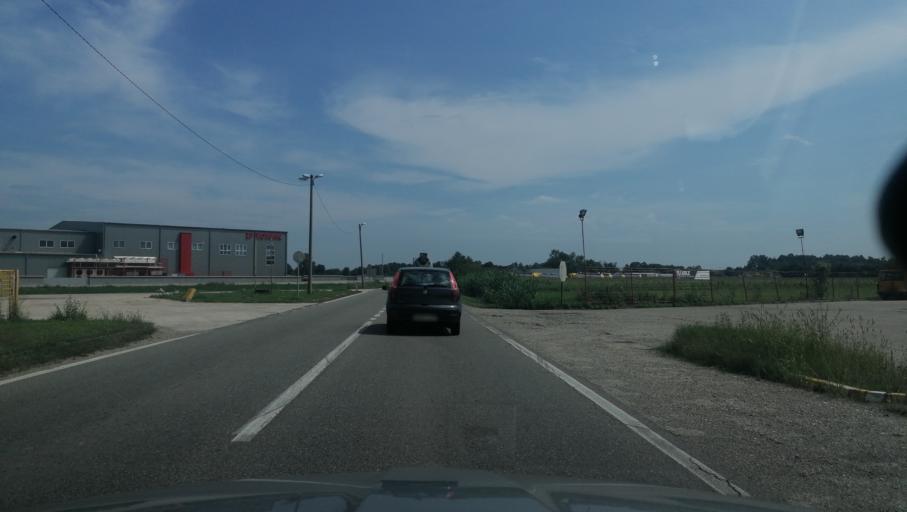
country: BA
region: Republika Srpska
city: Velika Obarska
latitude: 44.8273
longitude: 19.0317
